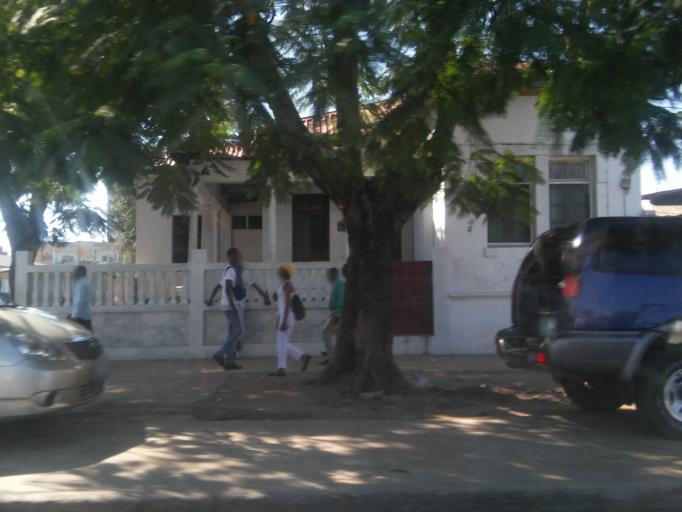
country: MZ
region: Maputo City
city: Maputo
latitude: -25.9606
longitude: 32.5651
